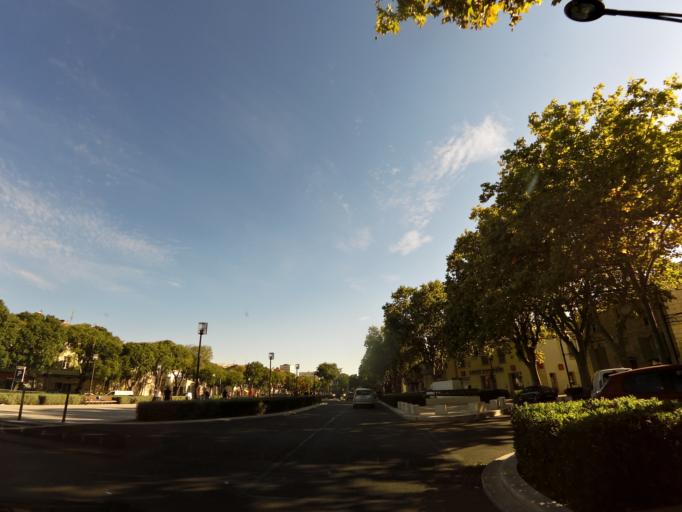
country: FR
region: Languedoc-Roussillon
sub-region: Departement du Gard
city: Nimes
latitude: 43.8368
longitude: 4.3503
